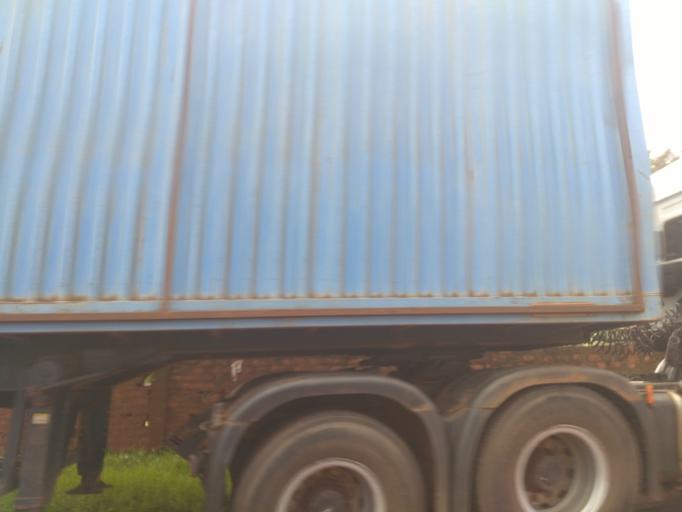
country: UG
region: Eastern Region
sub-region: Jinja District
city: Jinja
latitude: 0.4380
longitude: 33.2136
